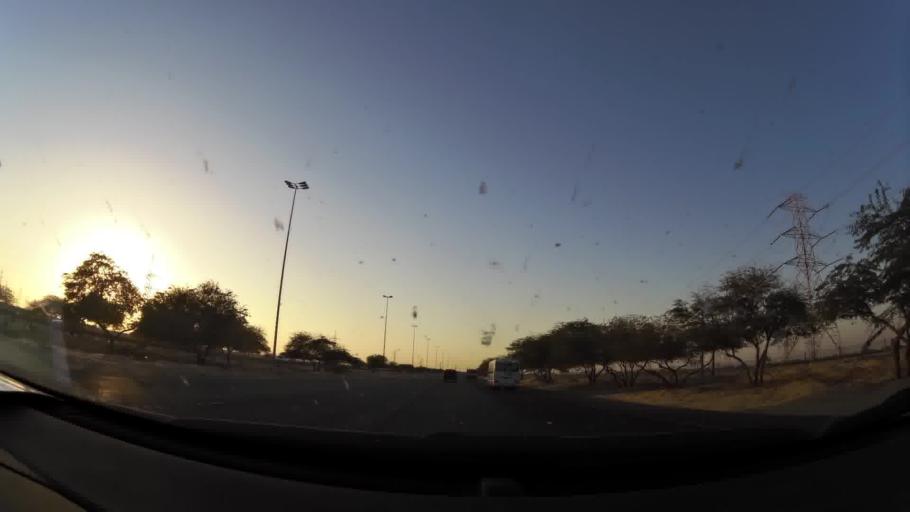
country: KW
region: Al Ahmadi
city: Al Fahahil
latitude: 28.9351
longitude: 48.1647
